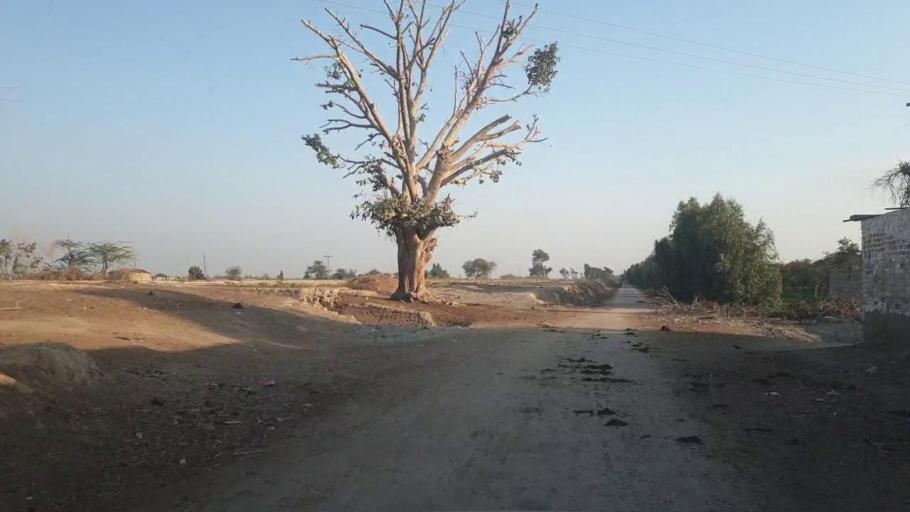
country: PK
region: Sindh
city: Chambar
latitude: 25.2931
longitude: 68.8935
